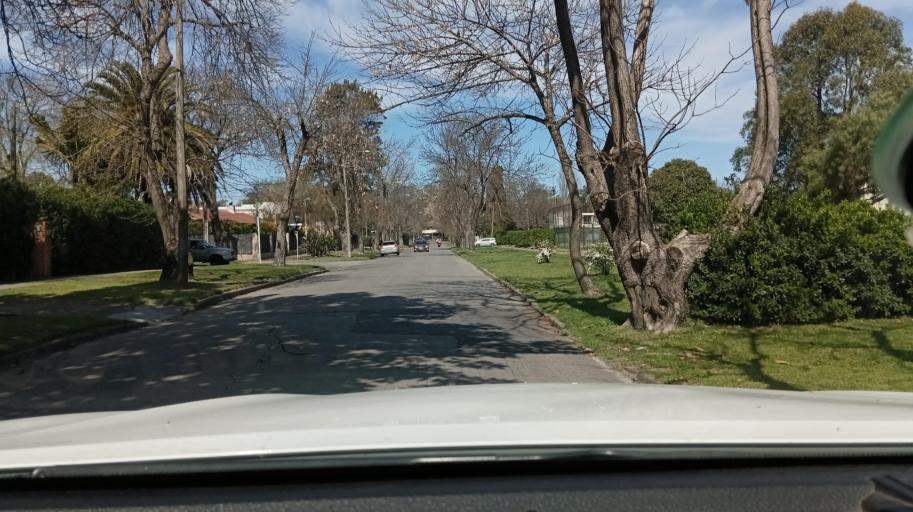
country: UY
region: Canelones
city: Paso de Carrasco
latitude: -34.8841
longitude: -56.0650
